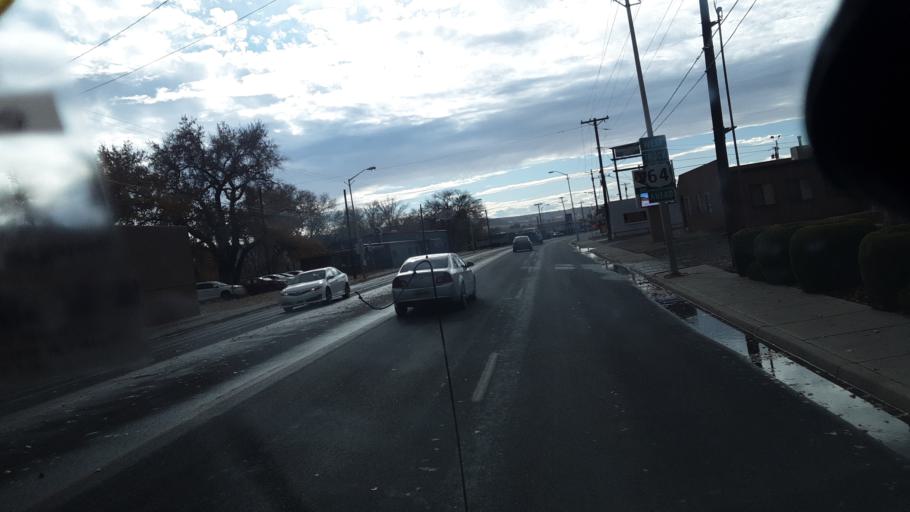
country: US
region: New Mexico
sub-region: San Juan County
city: Farmington
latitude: 36.7322
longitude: -108.1946
